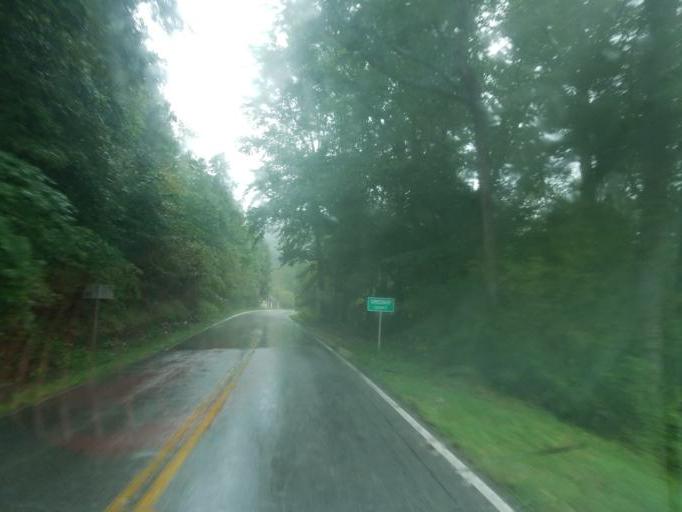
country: US
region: Kentucky
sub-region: Carter County
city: Grayson
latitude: 38.4651
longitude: -83.0516
